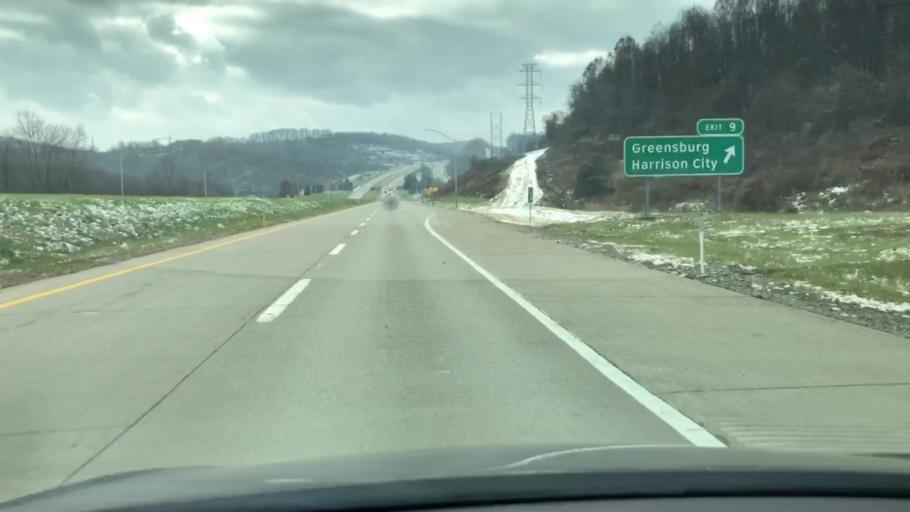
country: US
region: Pennsylvania
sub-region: Westmoreland County
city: Jeannette
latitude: 40.3516
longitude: -79.5643
